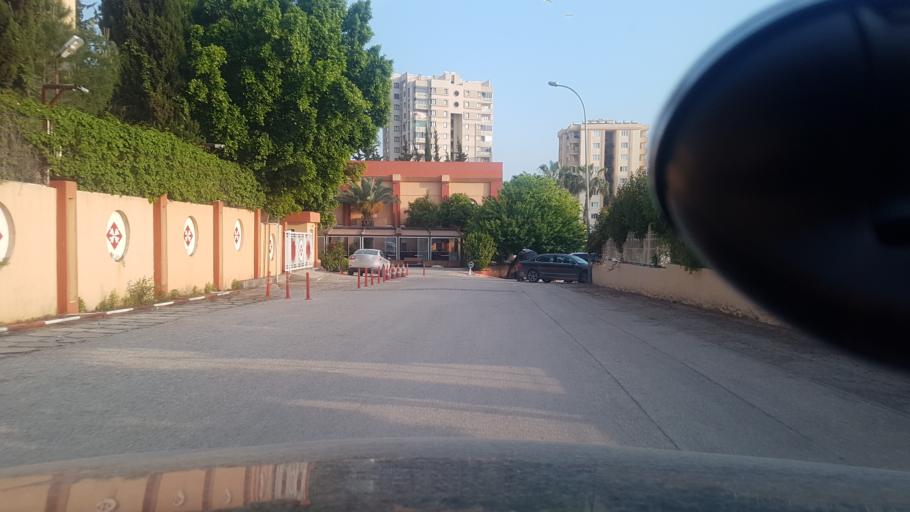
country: TR
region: Adana
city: Seyhan
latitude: 37.0457
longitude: 35.2749
